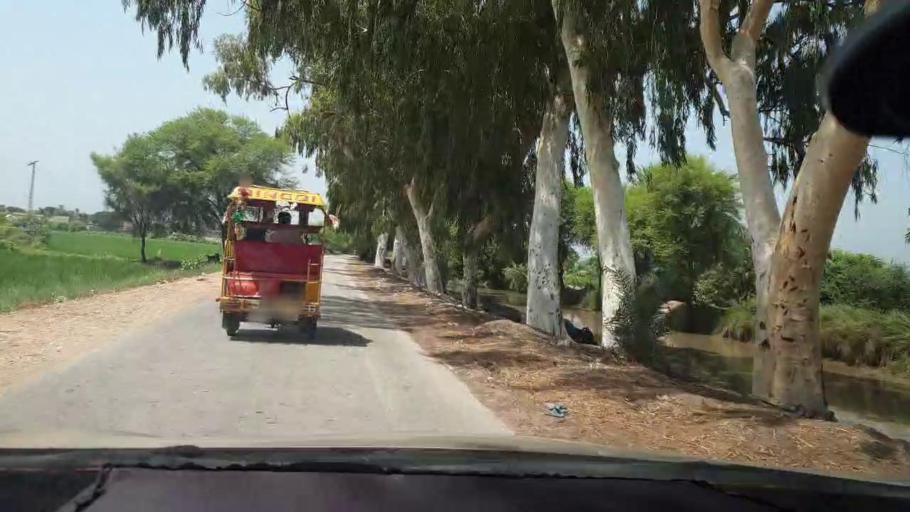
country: PK
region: Sindh
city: Kambar
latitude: 27.6343
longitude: 67.9852
